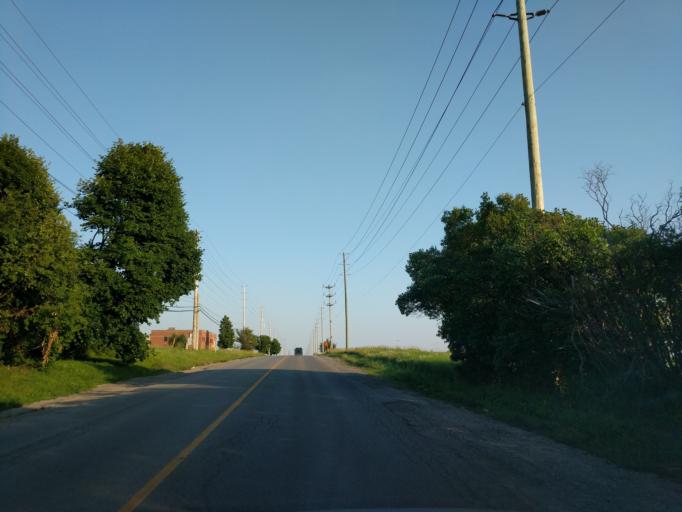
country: CA
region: Ontario
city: Oshawa
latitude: 43.8800
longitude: -78.8881
